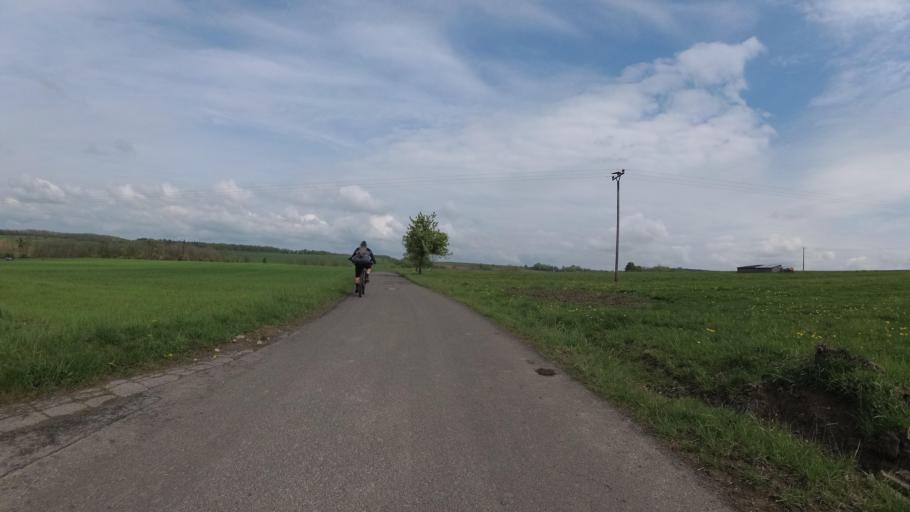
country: DE
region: Saarland
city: Merzig
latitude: 49.3832
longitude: 6.5925
